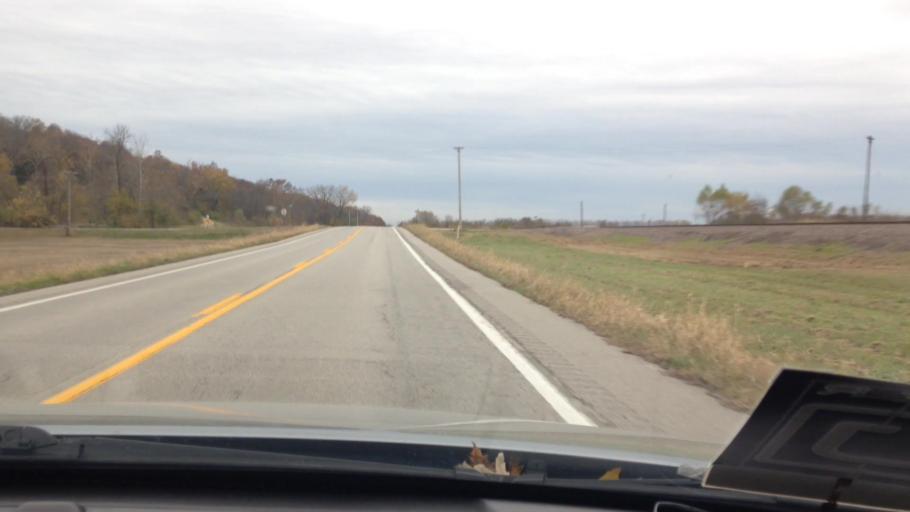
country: US
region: Kansas
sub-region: Leavenworth County
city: Leavenworth
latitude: 39.3291
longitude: -94.8577
